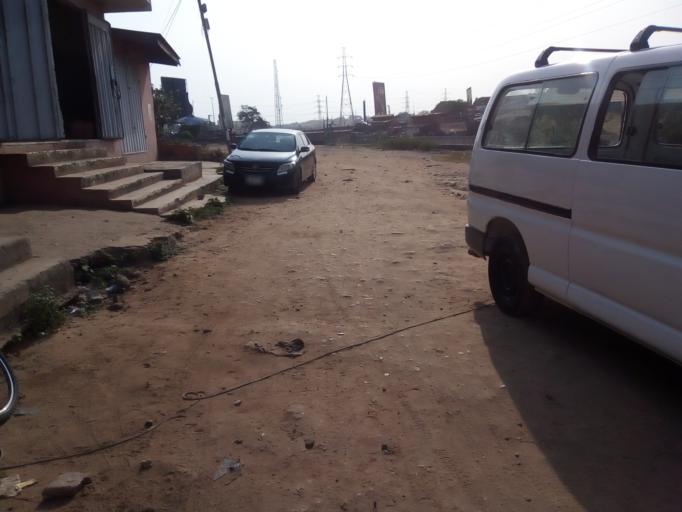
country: GH
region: Greater Accra
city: Accra
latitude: 5.5863
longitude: -0.2164
